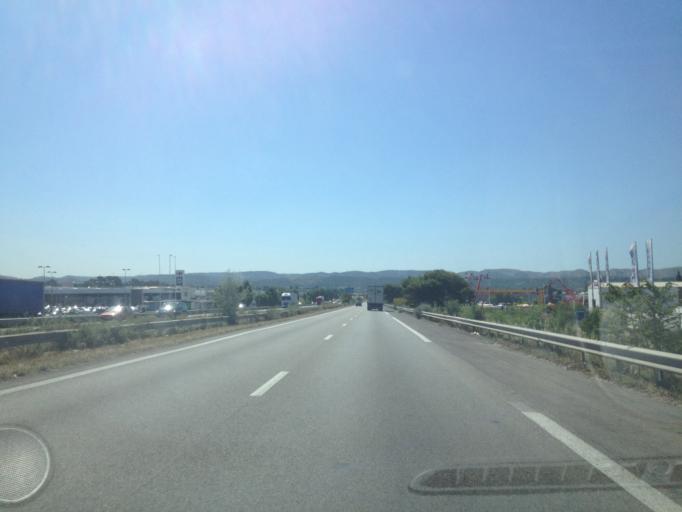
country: FR
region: Provence-Alpes-Cote d'Azur
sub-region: Departement des Bouches-du-Rhone
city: Saint-Victoret
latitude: 43.4346
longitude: 5.2551
